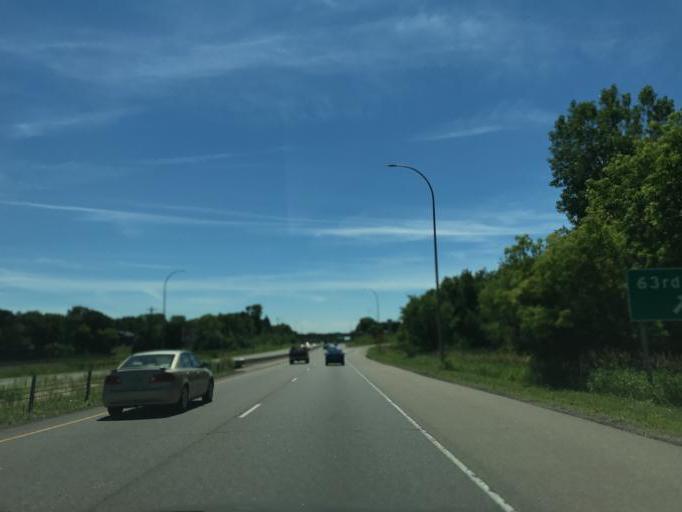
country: US
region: Minnesota
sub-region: Hennepin County
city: New Hope
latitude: 45.0732
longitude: -93.4017
